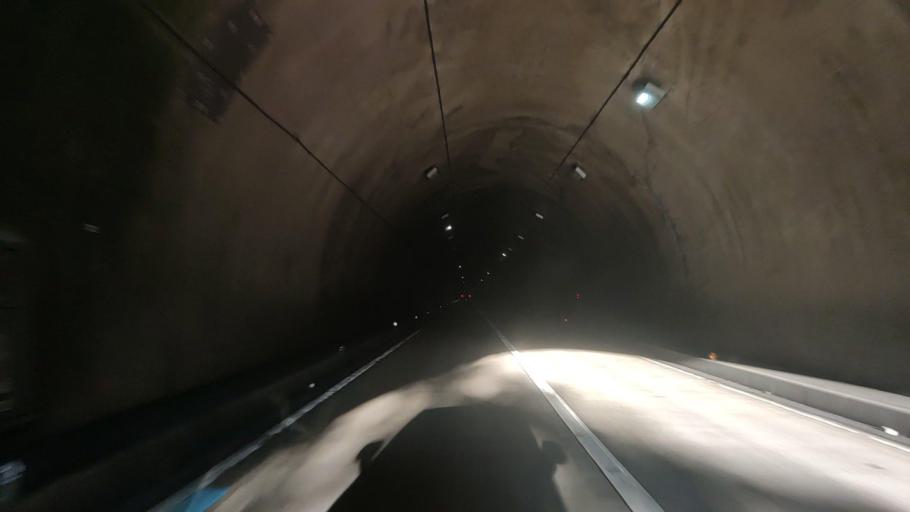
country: JP
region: Wakayama
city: Tanabe
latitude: 33.8143
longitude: 135.5788
